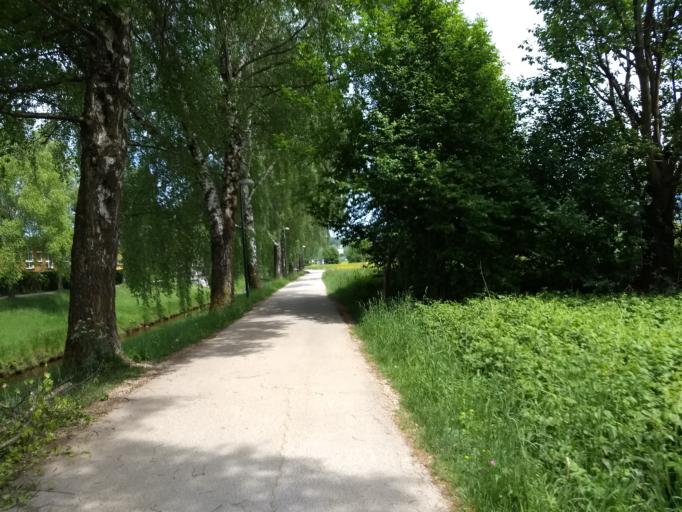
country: AT
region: Salzburg
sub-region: Salzburg Stadt
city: Salzburg
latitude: 47.7846
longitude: 13.0178
